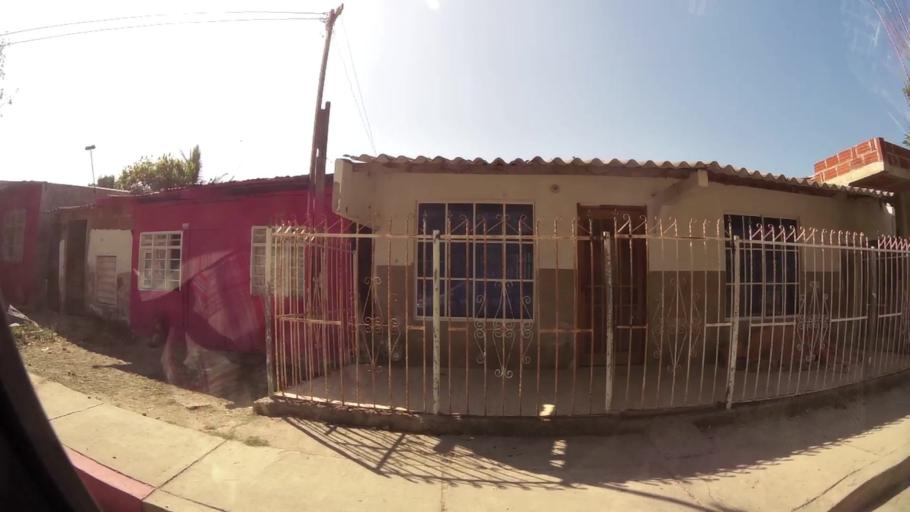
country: CO
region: Bolivar
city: Cartagena
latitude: 10.4142
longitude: -75.5085
